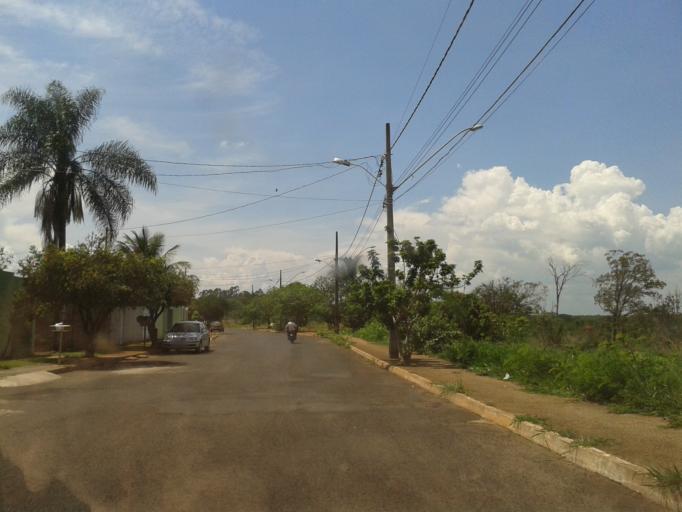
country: BR
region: Minas Gerais
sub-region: Araguari
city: Araguari
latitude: -18.6734
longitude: -48.1854
